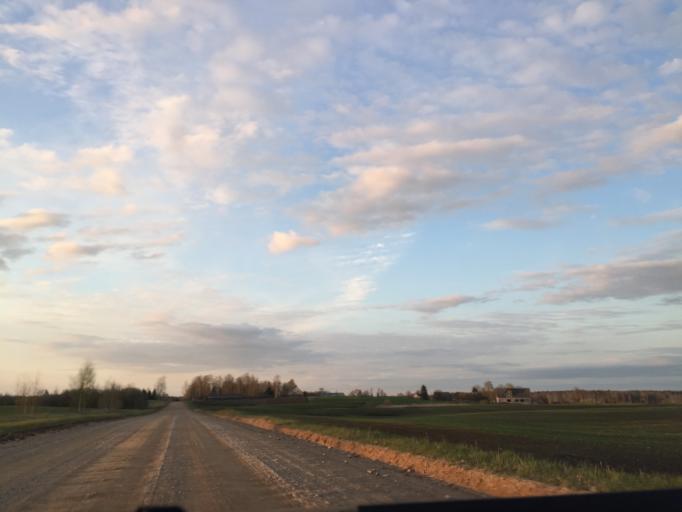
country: LV
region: Gulbenes Rajons
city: Gulbene
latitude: 57.2046
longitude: 26.7783
